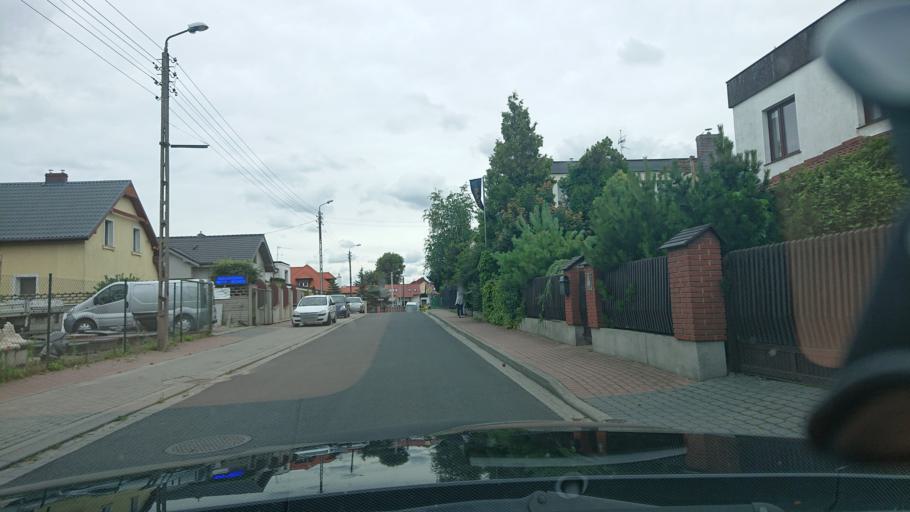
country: PL
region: Greater Poland Voivodeship
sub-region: Powiat gnieznienski
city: Gniezno
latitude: 52.5193
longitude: 17.6123
